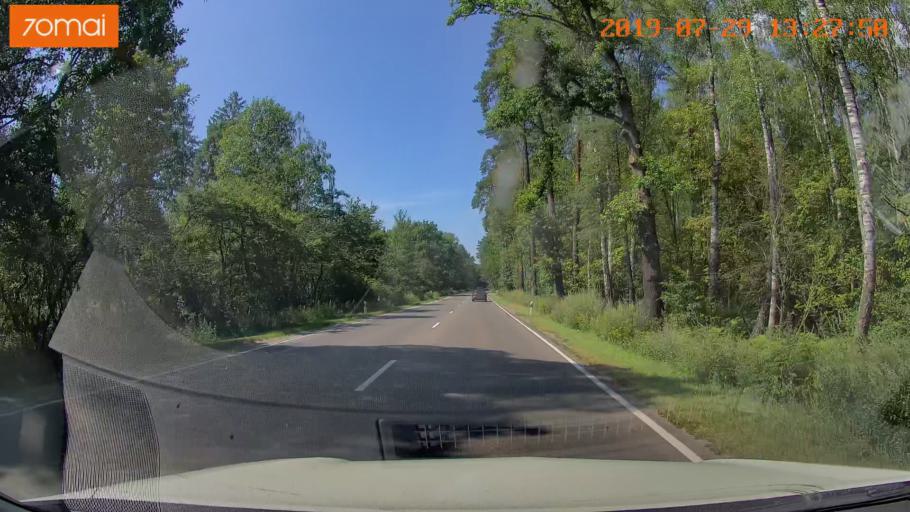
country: RU
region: Kaliningrad
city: Vzmorye
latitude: 54.7047
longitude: 20.2928
